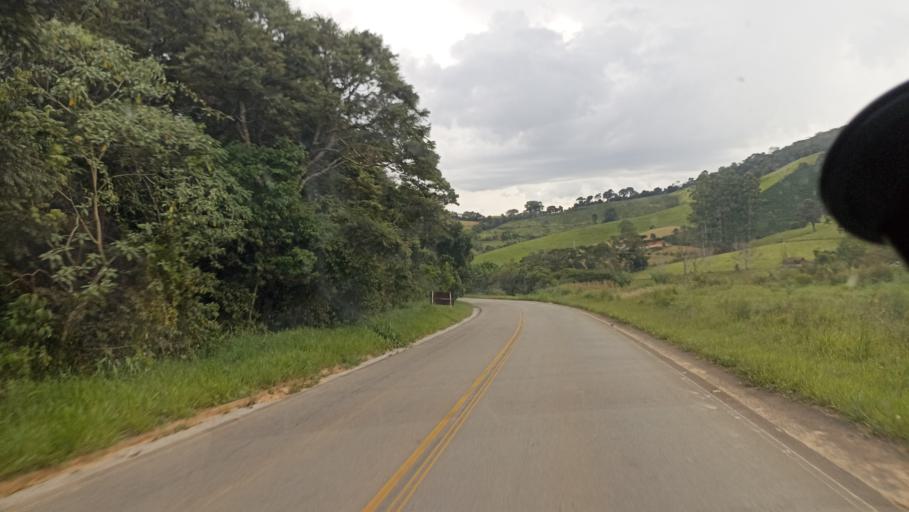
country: BR
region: Minas Gerais
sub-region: Cruzilia
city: Cruzilia
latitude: -21.8810
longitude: -44.8140
